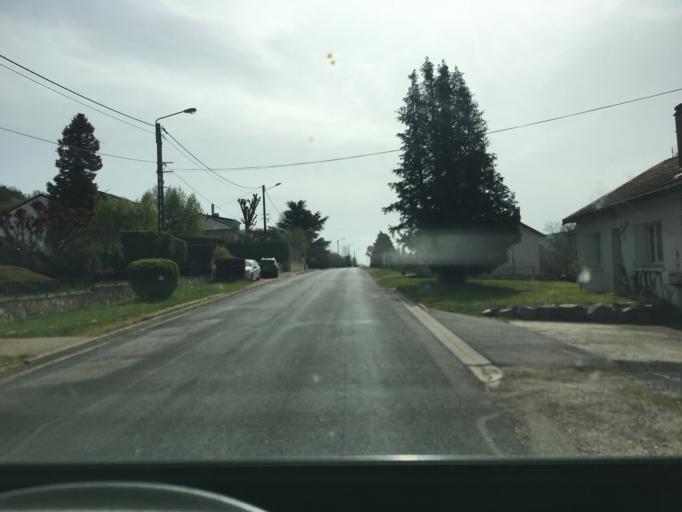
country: FR
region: Lorraine
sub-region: Departement de Meurthe-et-Moselle
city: Chaligny
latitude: 48.6297
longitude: 6.0516
